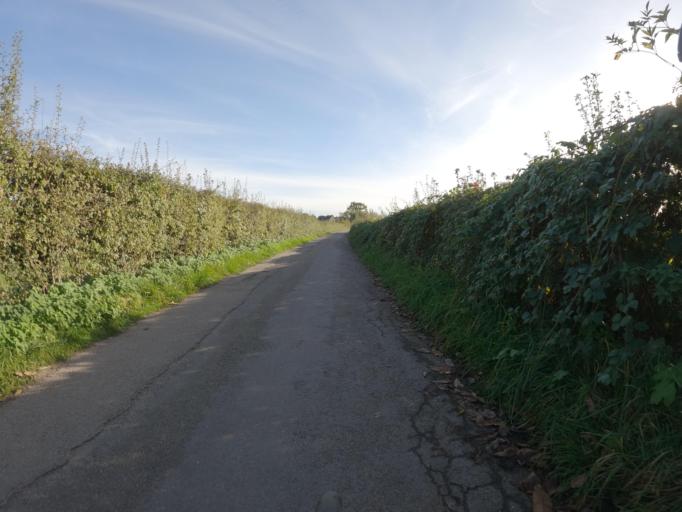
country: DE
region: North Rhine-Westphalia
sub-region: Regierungsbezirk Koln
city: Aachen
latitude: 50.8182
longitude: 6.0841
